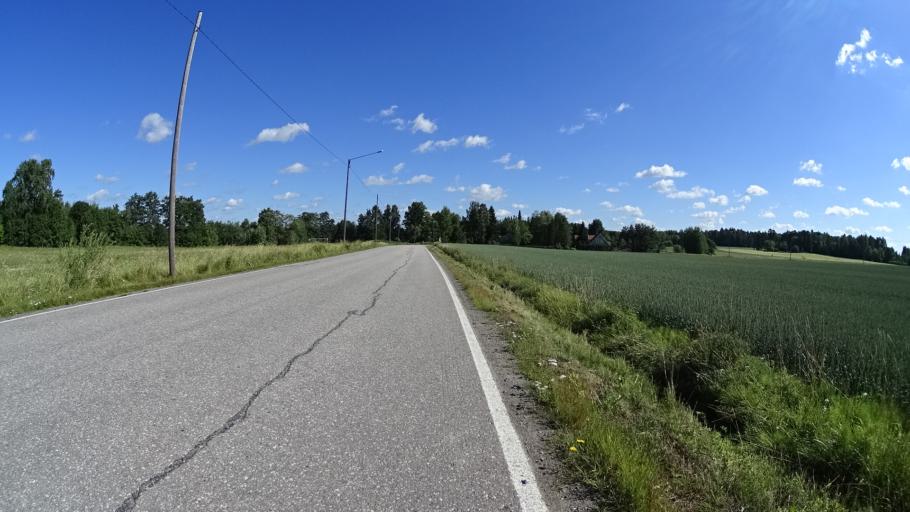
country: FI
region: Uusimaa
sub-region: Helsinki
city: Jaervenpaeae
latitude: 60.4417
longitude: 25.0710
